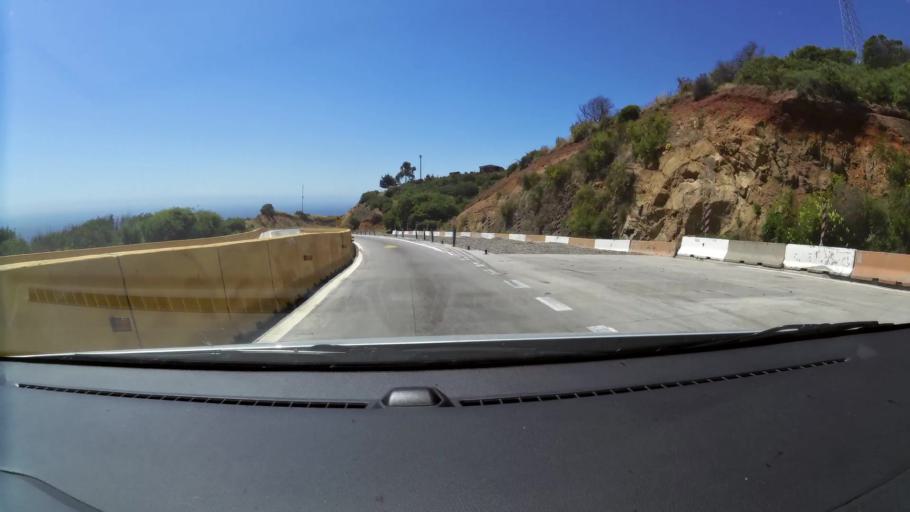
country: CL
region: Valparaiso
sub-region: Provincia de Valparaiso
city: Valparaiso
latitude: -33.0501
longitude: -71.6567
